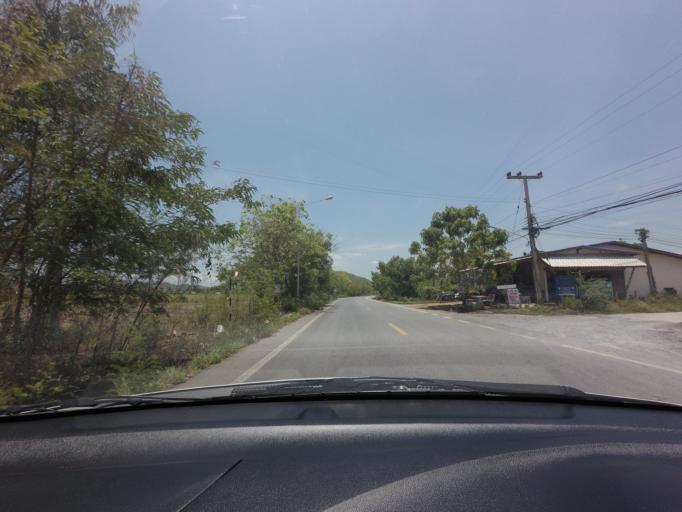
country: TH
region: Suphan Buri
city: Dan Chang
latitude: 14.8501
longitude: 99.7035
